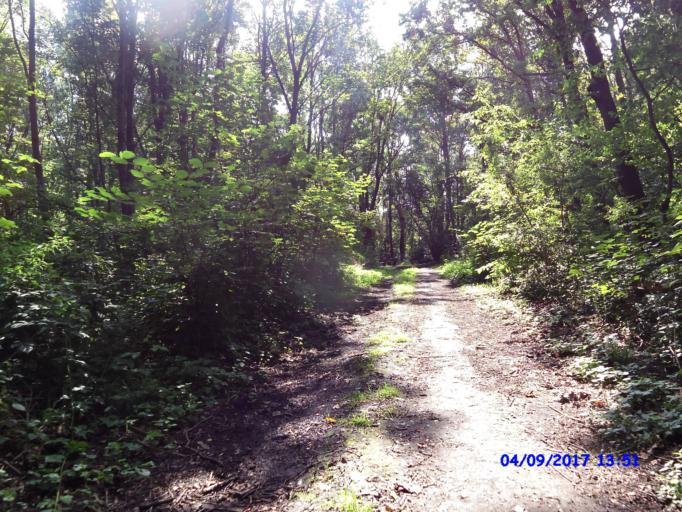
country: DE
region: Saxony
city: Taucha
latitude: 51.3552
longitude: 12.4683
